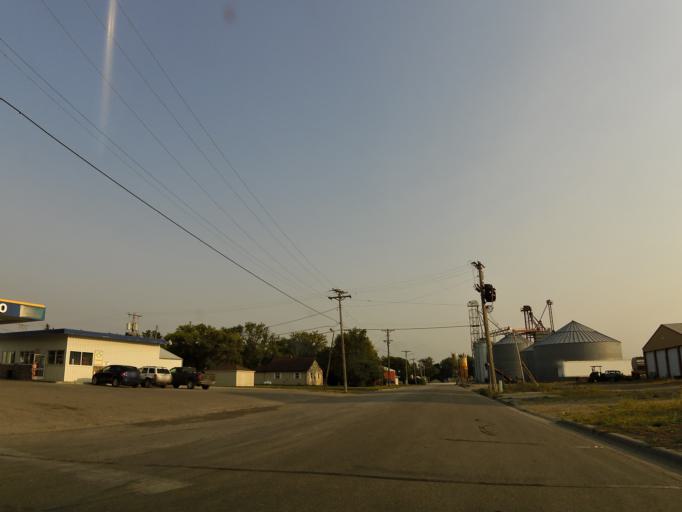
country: US
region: North Dakota
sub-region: Traill County
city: Mayville
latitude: 47.4980
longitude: -97.3227
